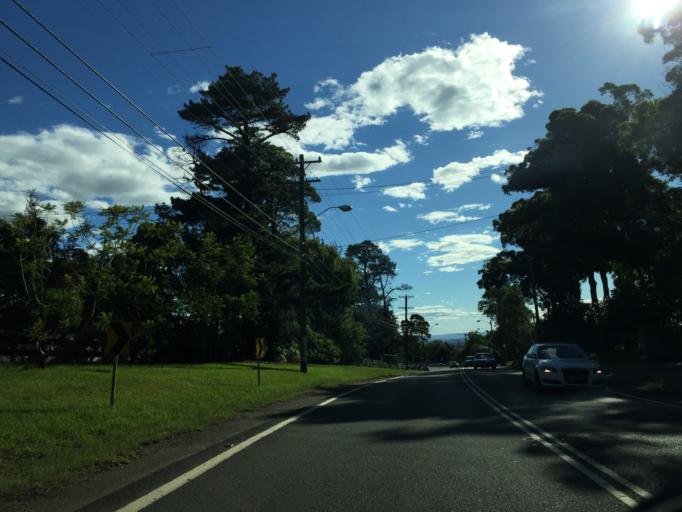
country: AU
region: New South Wales
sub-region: The Hills Shire
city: Glenhaven
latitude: -33.7049
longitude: 151.0136
